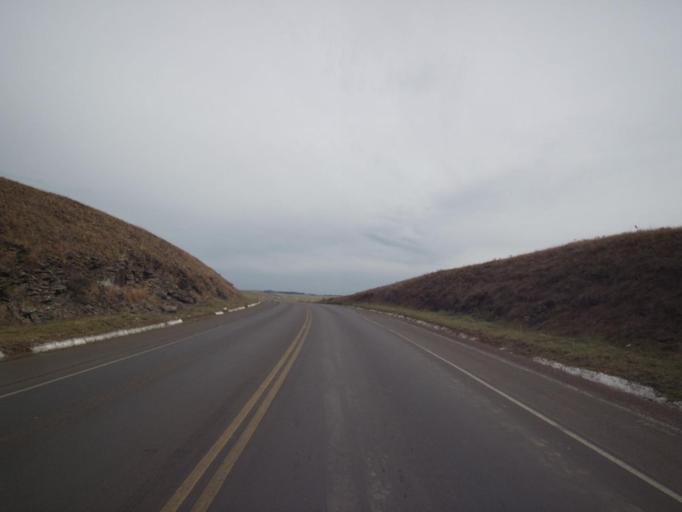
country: BR
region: Parana
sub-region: Palmas
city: Palmas
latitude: -26.7482
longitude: -51.6615
